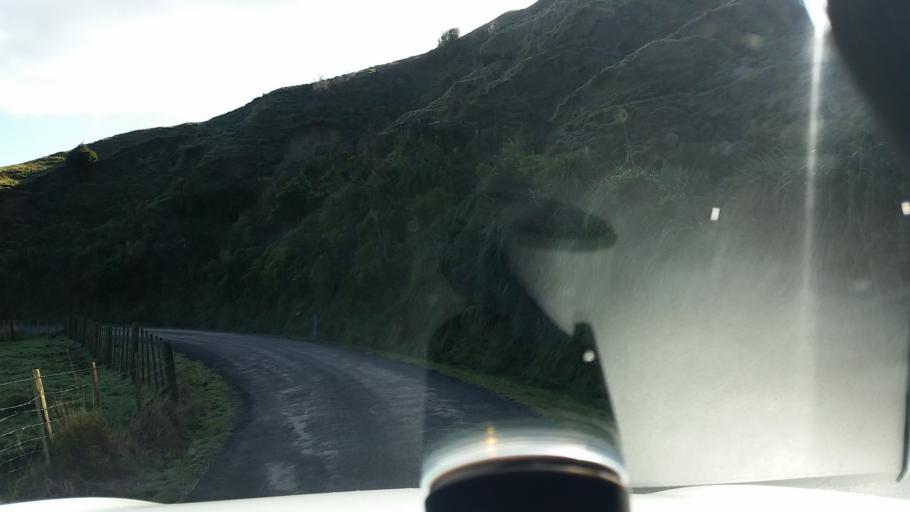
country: NZ
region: Taranaki
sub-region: South Taranaki District
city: Eltham
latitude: -39.4126
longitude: 174.5298
